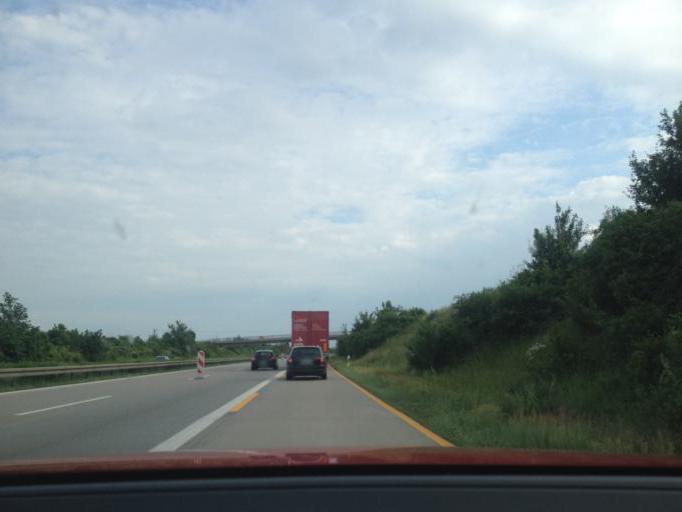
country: DE
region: Saxony-Anhalt
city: Nauendorf
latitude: 51.6205
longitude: 11.8678
